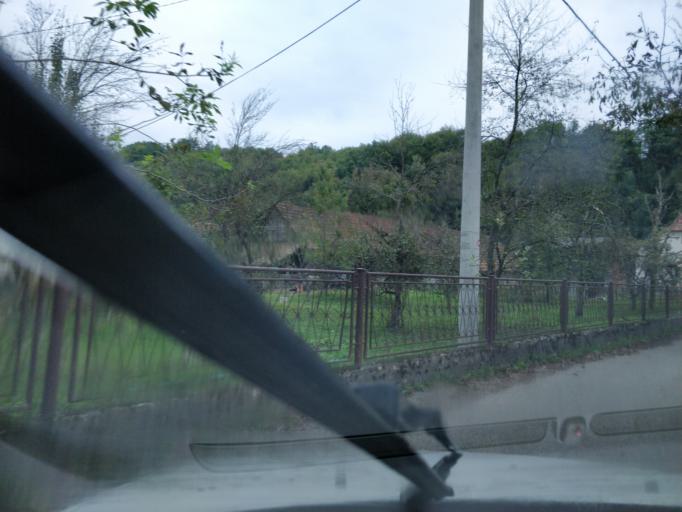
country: HR
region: Krapinsko-Zagorska
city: Oroslavje
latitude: 45.9397
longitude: 15.9183
